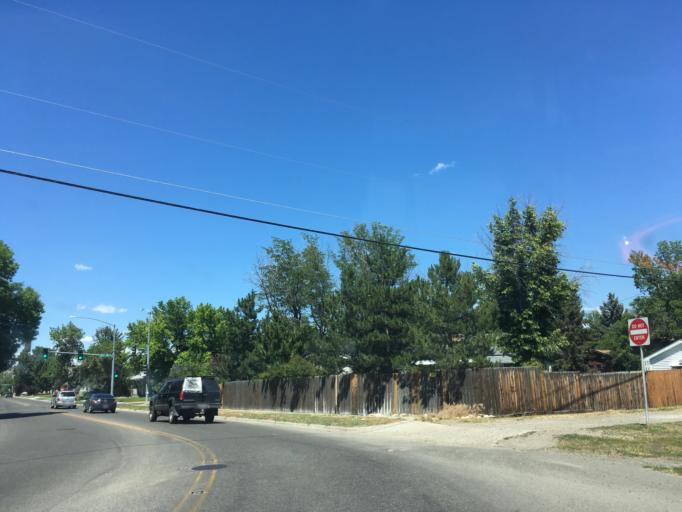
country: US
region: Montana
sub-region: Yellowstone County
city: Billings
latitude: 45.7732
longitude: -108.5643
